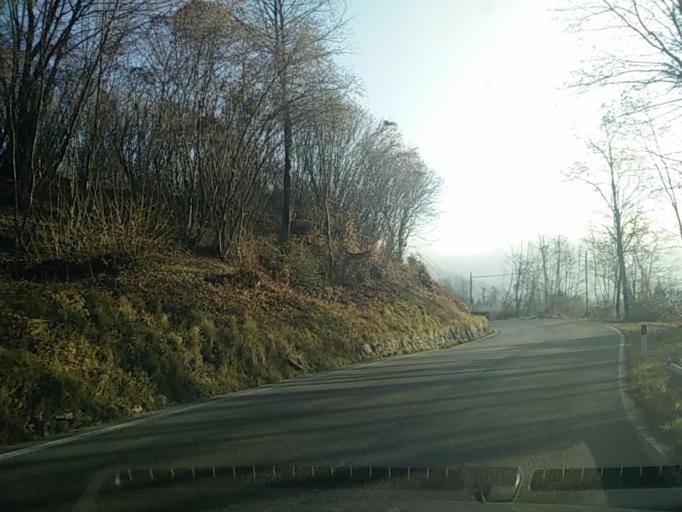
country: IT
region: Veneto
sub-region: Provincia di Belluno
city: Trichiana
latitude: 46.0470
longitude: 12.1564
